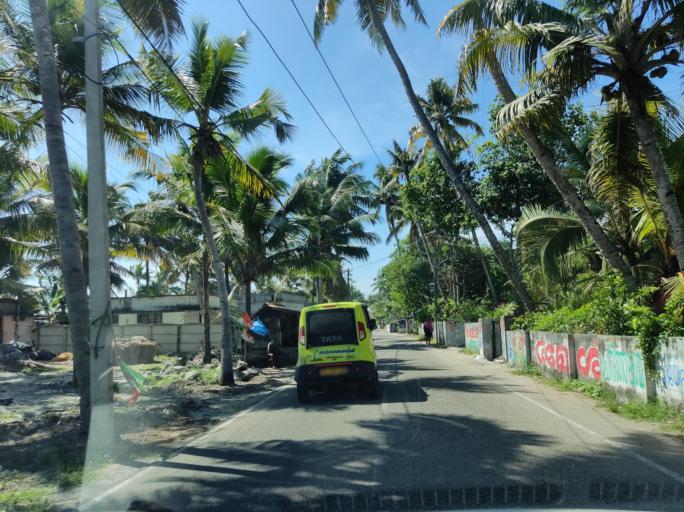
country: IN
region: Kerala
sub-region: Alappuzha
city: Kayankulam
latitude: 9.2245
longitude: 76.4233
